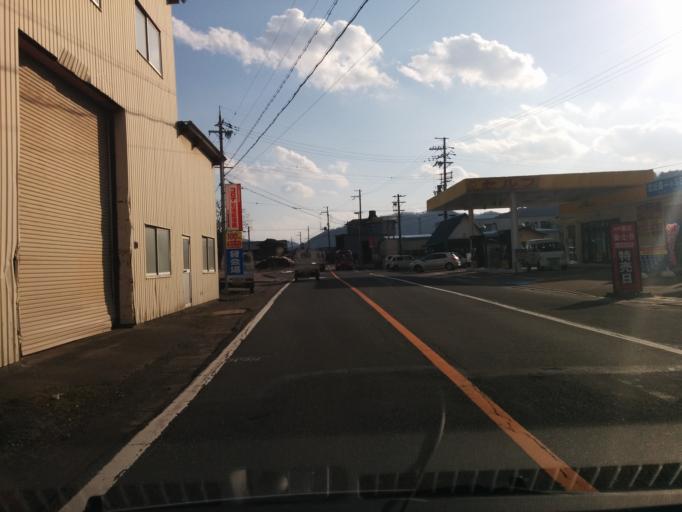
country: JP
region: Kyoto
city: Ayabe
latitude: 35.3398
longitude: 135.2166
